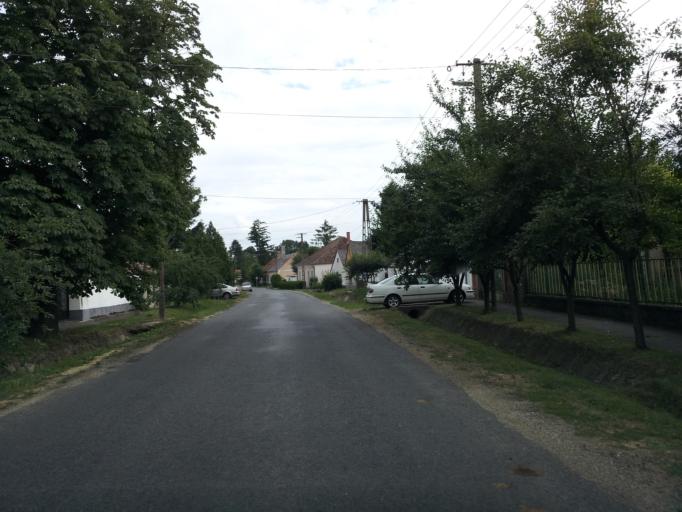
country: HU
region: Vas
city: Janoshaza
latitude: 47.1423
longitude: 17.1033
